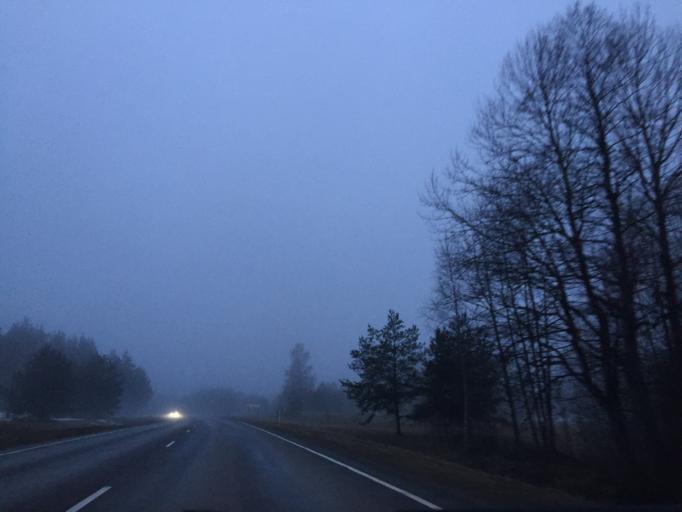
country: EE
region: Laeaene
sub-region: Lihula vald
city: Lihula
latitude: 58.6414
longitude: 23.6952
